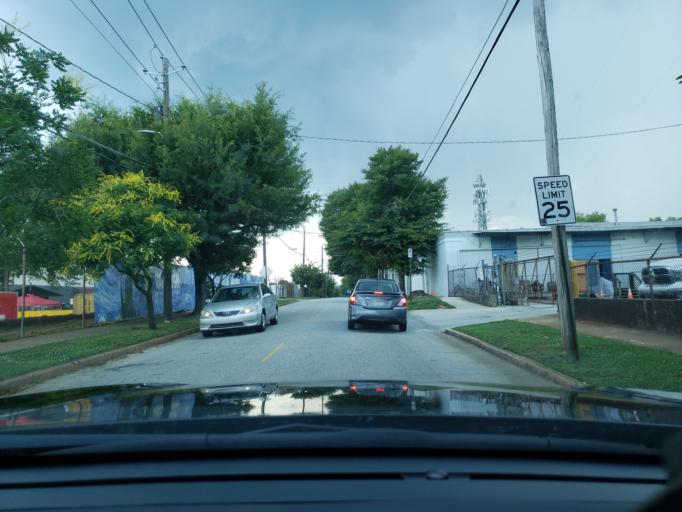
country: US
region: Georgia
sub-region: DeKalb County
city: Druid Hills
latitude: 33.7597
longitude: -84.3292
